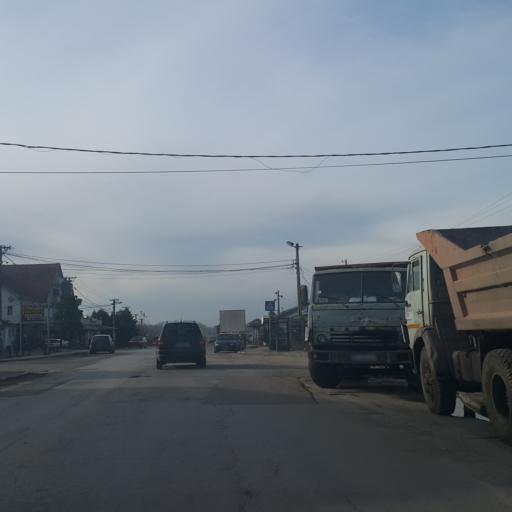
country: RS
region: Central Serbia
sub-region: Belgrade
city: Lazarevac
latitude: 44.3991
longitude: 20.3700
